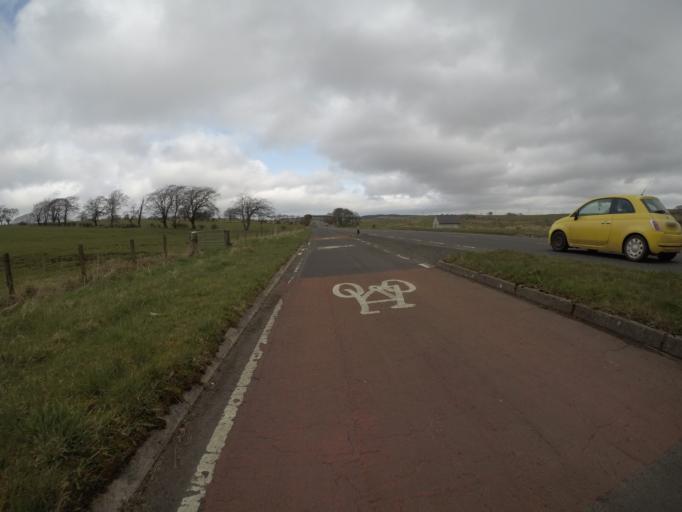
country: GB
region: Scotland
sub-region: East Ayrshire
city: Galston
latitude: 55.6838
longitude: -4.4189
